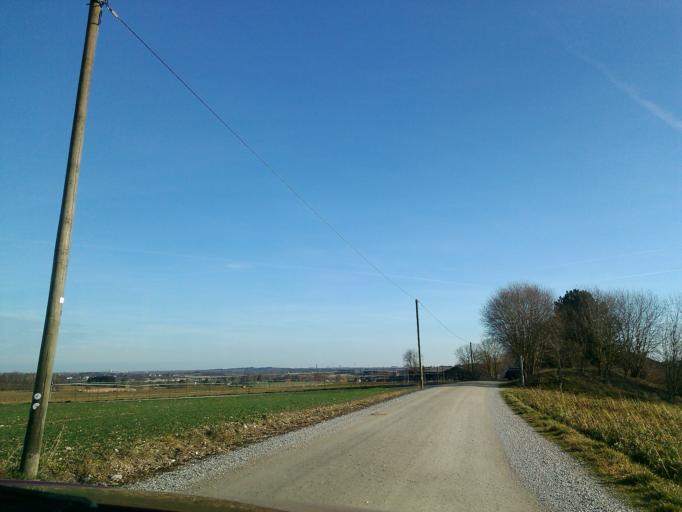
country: DE
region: Bavaria
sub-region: Upper Bavaria
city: Alling
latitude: 48.1424
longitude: 11.2856
